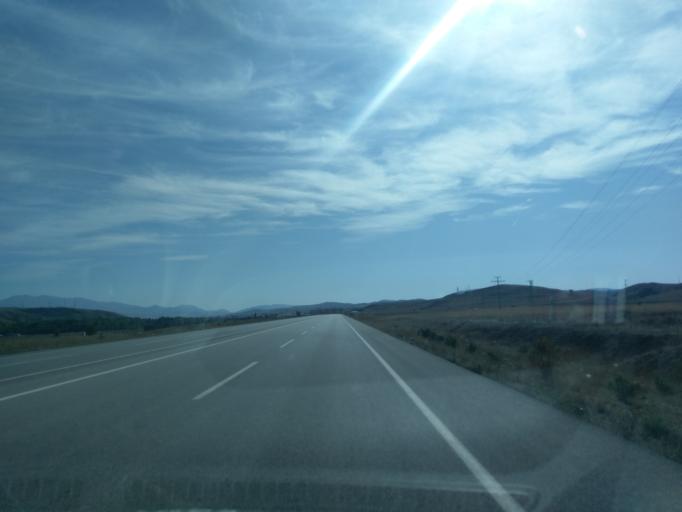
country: TR
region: Sivas
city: Imranli
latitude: 39.8736
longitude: 38.0875
